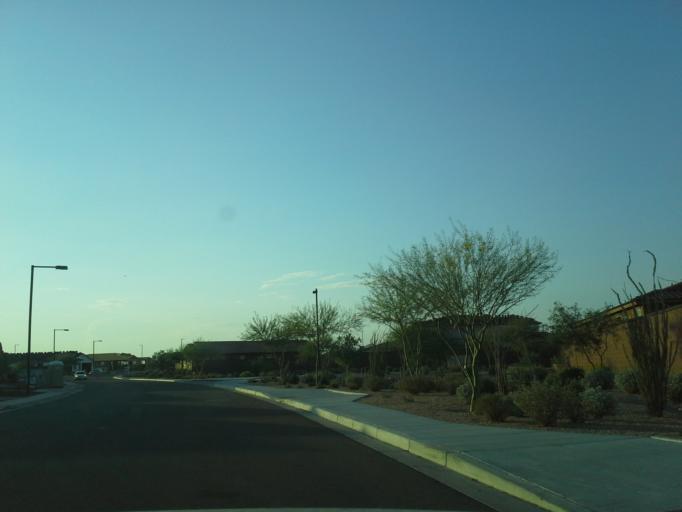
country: US
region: Arizona
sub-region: Maricopa County
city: Anthem
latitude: 33.7672
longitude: -112.1160
